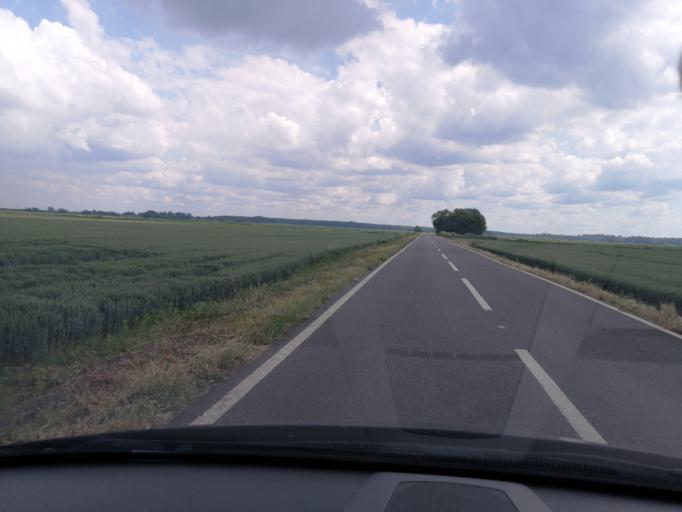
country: GB
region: England
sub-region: Cambridgeshire
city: Yaxley
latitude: 52.5073
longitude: -0.2577
